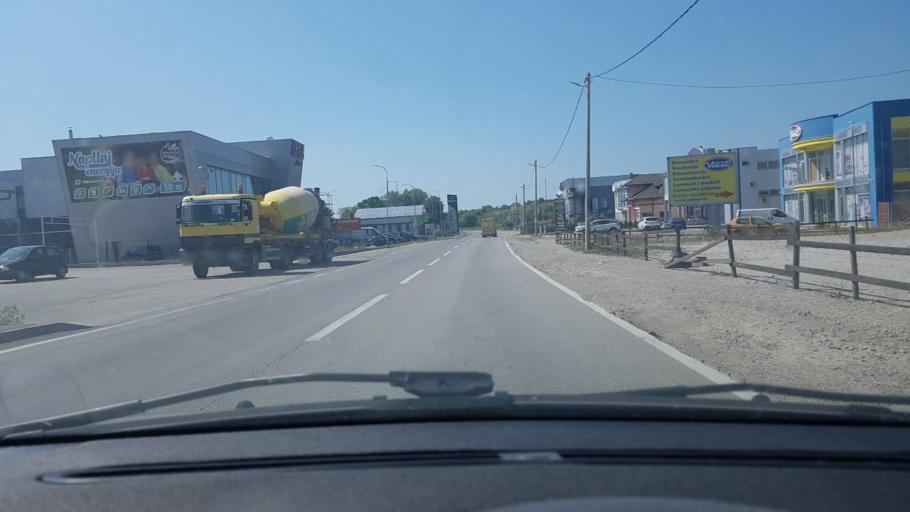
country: BA
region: Federation of Bosnia and Herzegovina
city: Bihac
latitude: 44.7957
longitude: 15.9202
